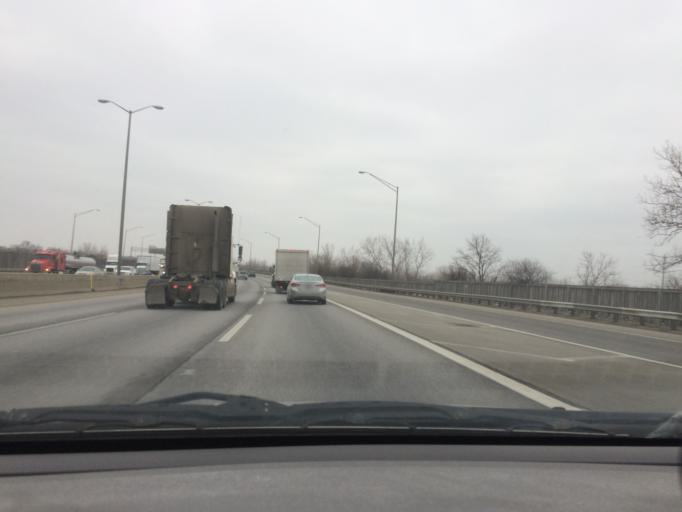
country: US
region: Illinois
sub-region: DuPage County
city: Glen Ellyn
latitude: 41.8554
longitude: -88.0408
